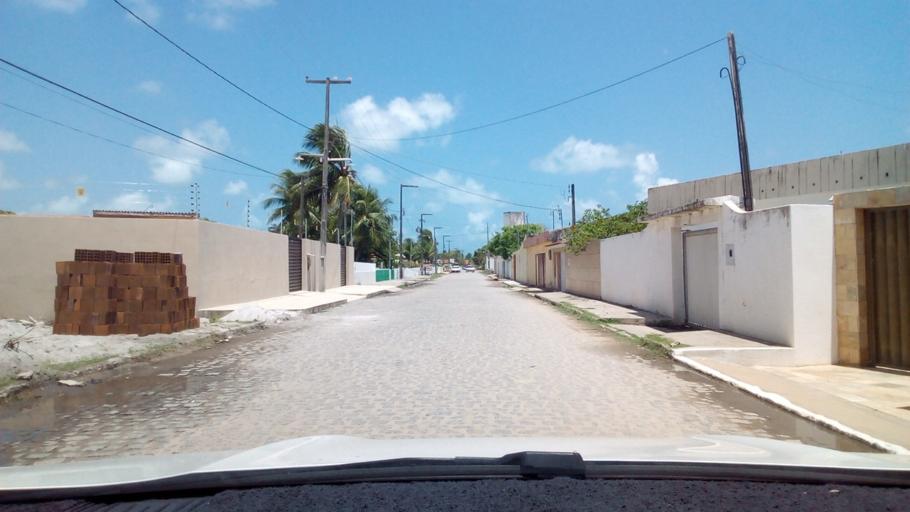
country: BR
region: Paraiba
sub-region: Pitimbu
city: Pitimbu
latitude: -7.5176
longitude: -34.8139
